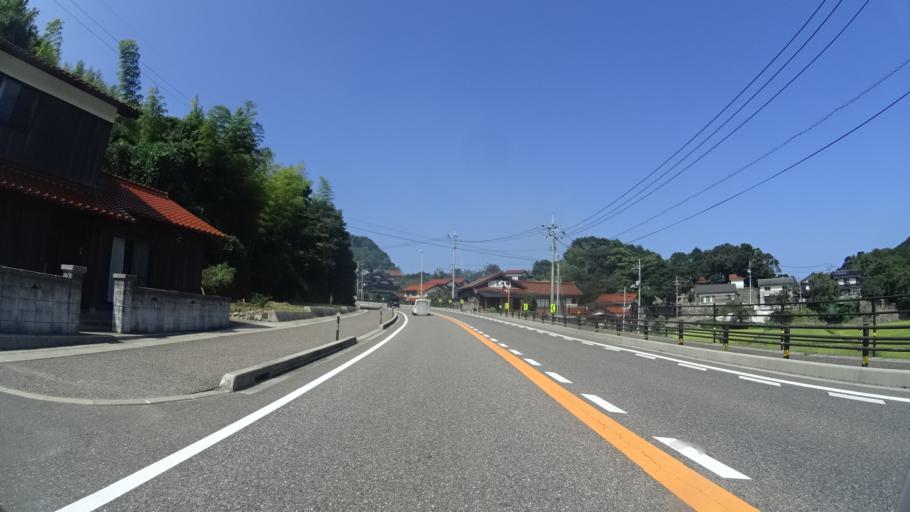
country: JP
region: Shimane
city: Masuda
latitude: 34.7563
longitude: 131.8959
